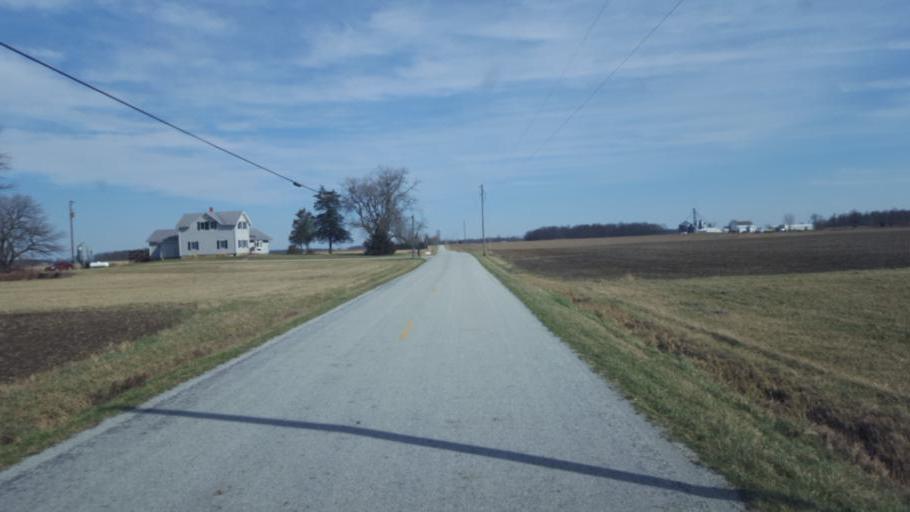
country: US
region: Ohio
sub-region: Hardin County
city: Kenton
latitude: 40.6575
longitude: -83.4870
